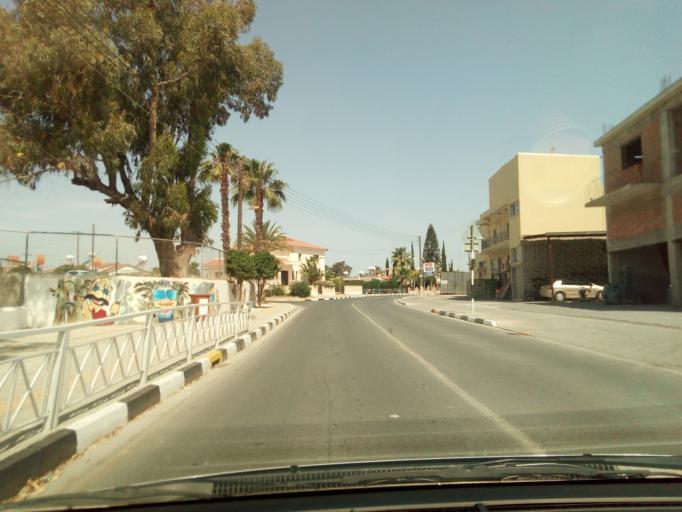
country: CY
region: Larnaka
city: Livadia
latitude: 34.9502
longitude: 33.6267
